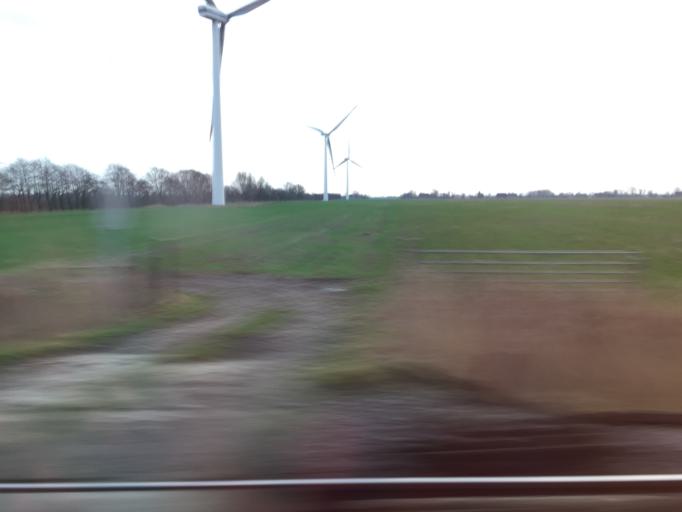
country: DE
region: Schleswig-Holstein
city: Krempdorf
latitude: 53.8225
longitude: 9.4692
